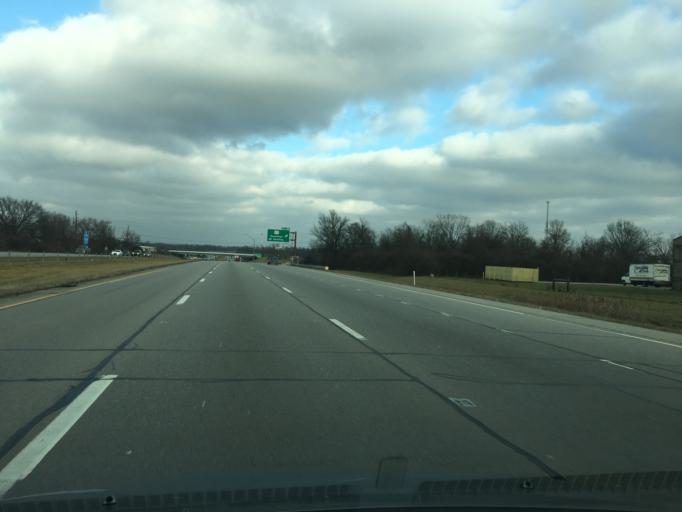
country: US
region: Ohio
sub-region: Hamilton County
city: Mount Healthy Heights
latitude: 39.2811
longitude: -84.5698
